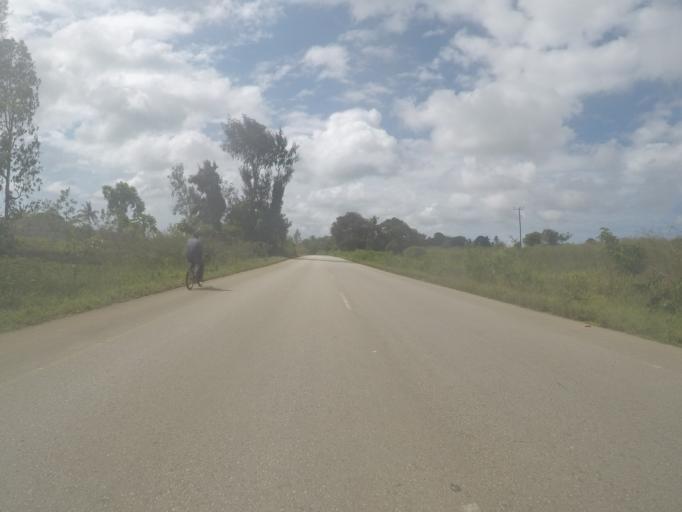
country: TZ
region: Zanzibar North
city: Kijini
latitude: -5.8474
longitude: 39.2837
